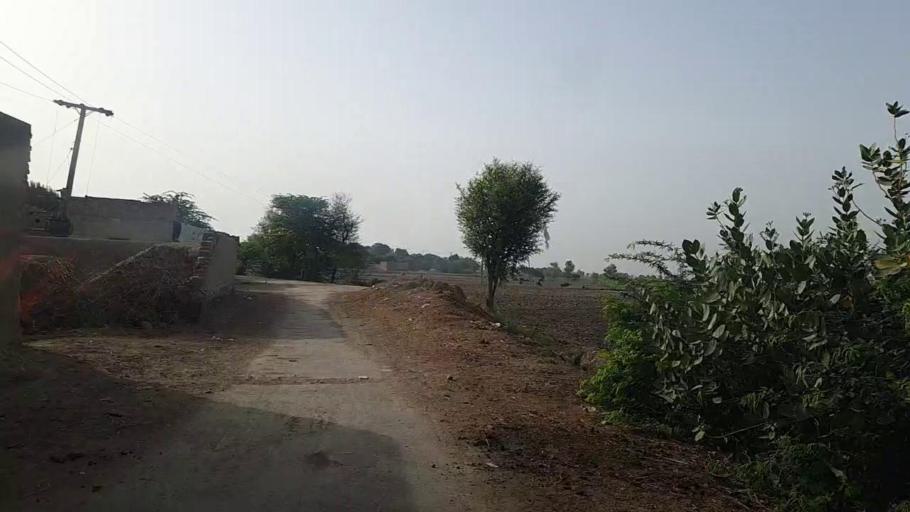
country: PK
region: Sindh
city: Khairpur Nathan Shah
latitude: 27.1107
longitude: 67.7892
